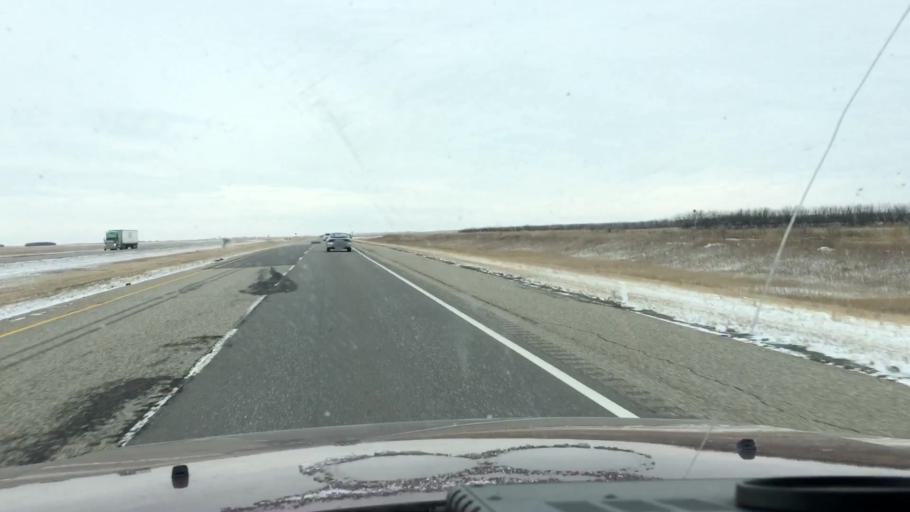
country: CA
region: Saskatchewan
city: Saskatoon
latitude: 51.4670
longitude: -106.2425
